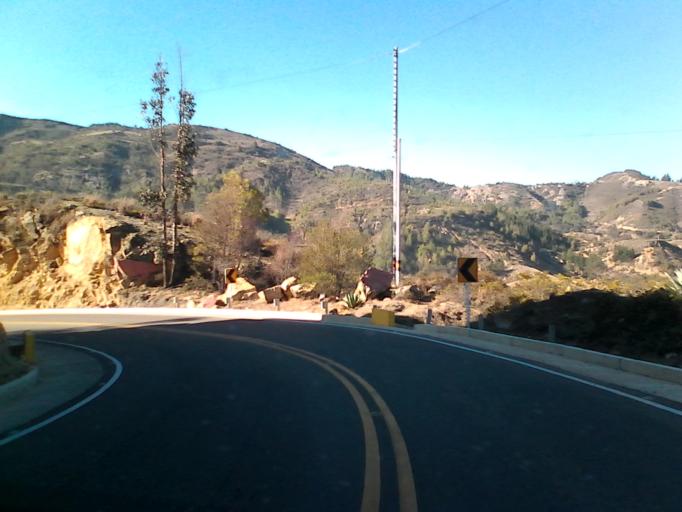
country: CO
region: Boyaca
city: Cucaita
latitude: 5.5424
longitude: -73.4459
